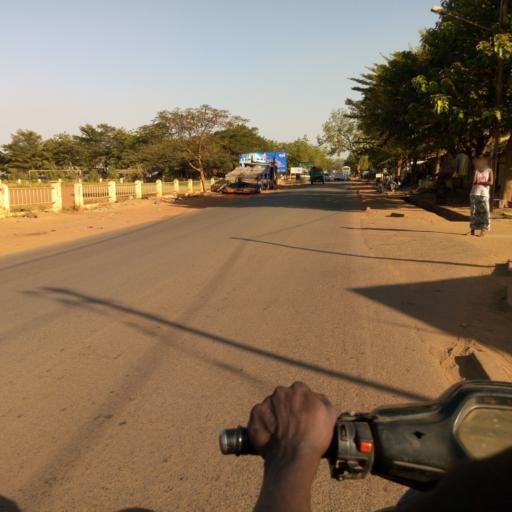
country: ML
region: Bamako
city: Bamako
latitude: 12.6515
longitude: -8.0149
